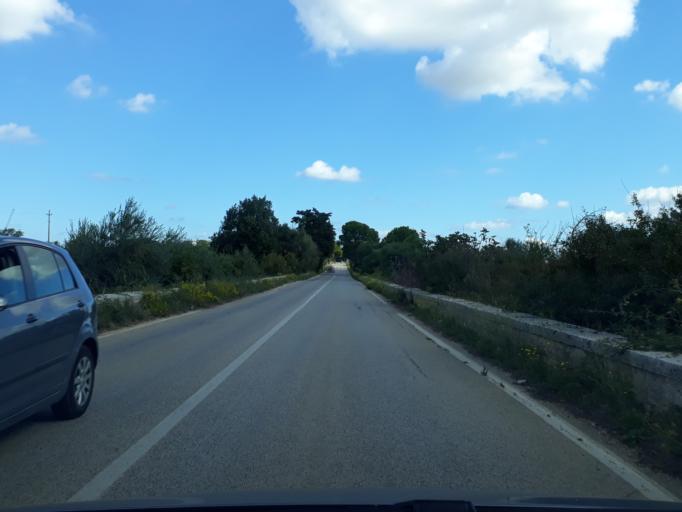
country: IT
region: Apulia
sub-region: Provincia di Bari
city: Rutigliano
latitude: 41.0212
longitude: 17.0261
